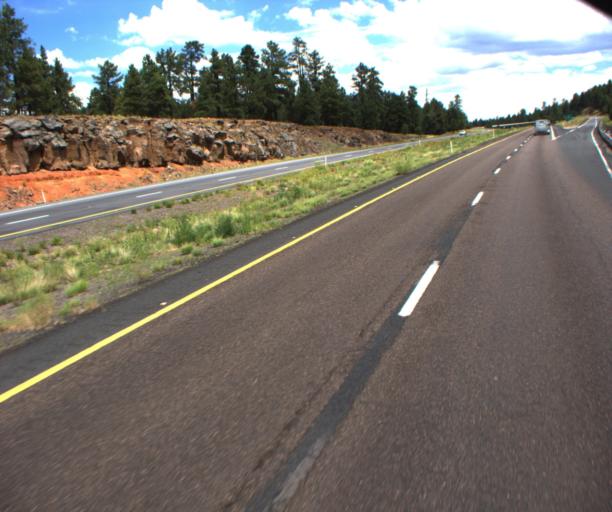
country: US
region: Arizona
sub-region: Coconino County
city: Mountainaire
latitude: 35.0454
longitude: -111.6846
